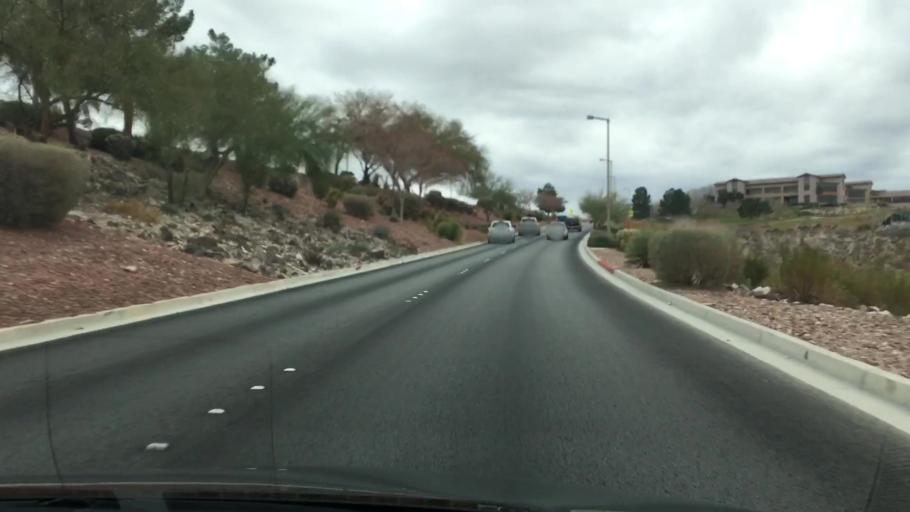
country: US
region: Nevada
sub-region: Clark County
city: Whitney
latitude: 35.9601
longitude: -115.0954
